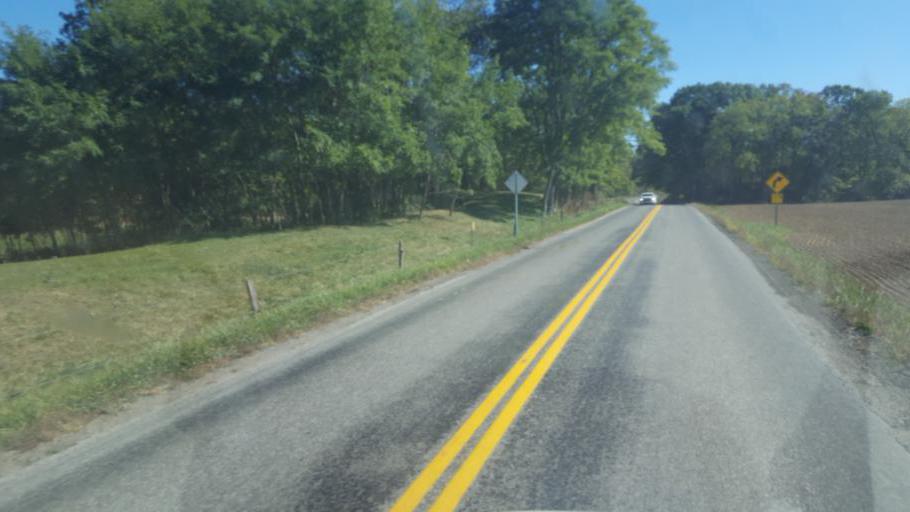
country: US
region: Ohio
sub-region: Wayne County
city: West Salem
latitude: 40.9096
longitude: -82.1591
